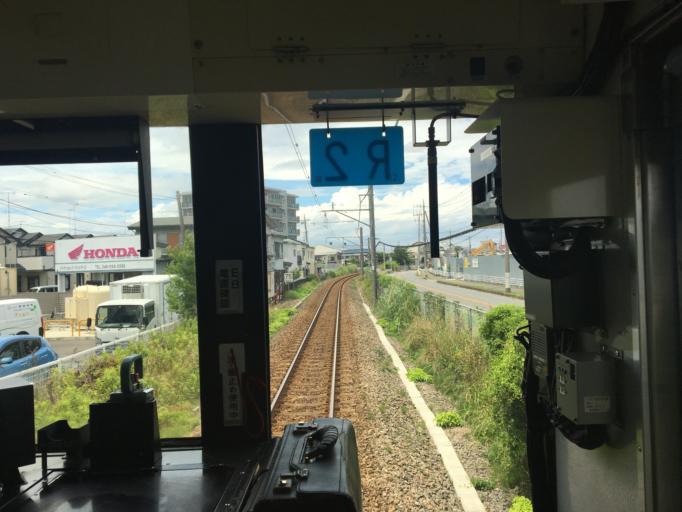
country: JP
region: Kanagawa
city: Atsugi
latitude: 35.4090
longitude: 139.3788
